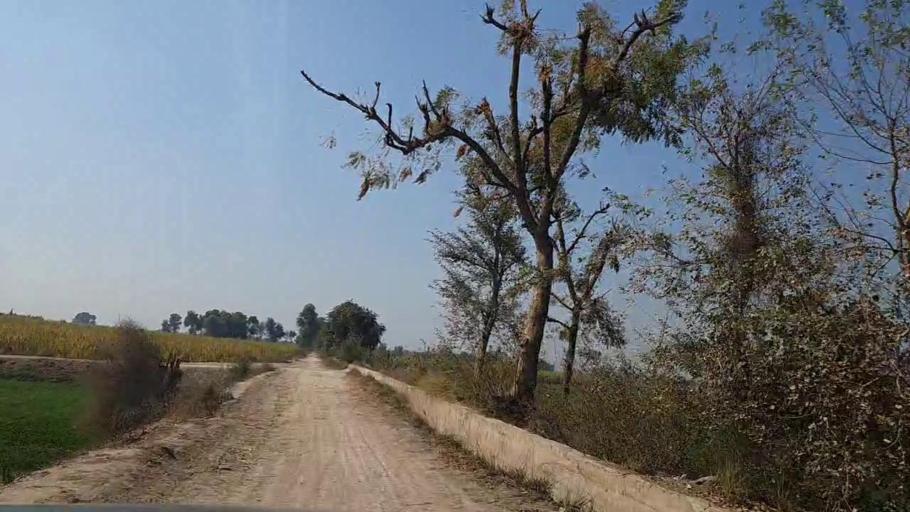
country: PK
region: Sindh
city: Daulatpur
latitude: 26.2904
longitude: 68.0652
